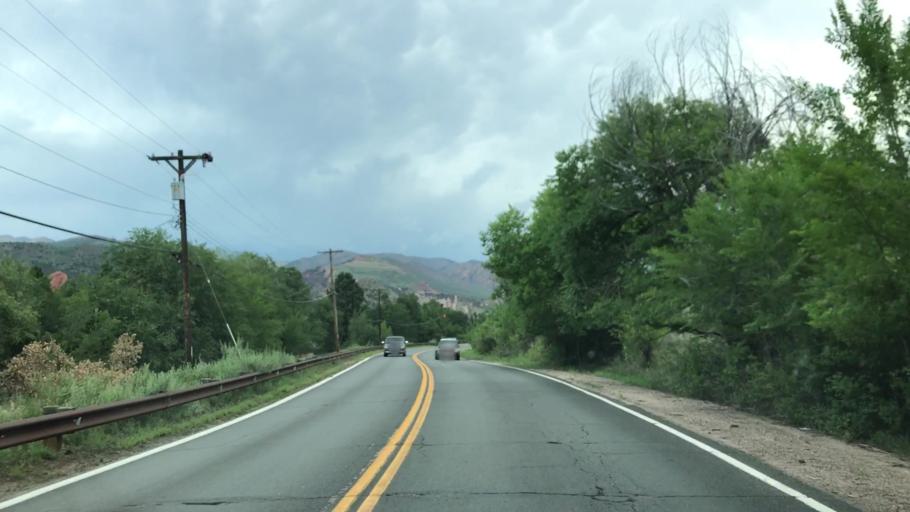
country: US
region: Colorado
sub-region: El Paso County
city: Manitou Springs
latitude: 38.8686
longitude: -104.8673
